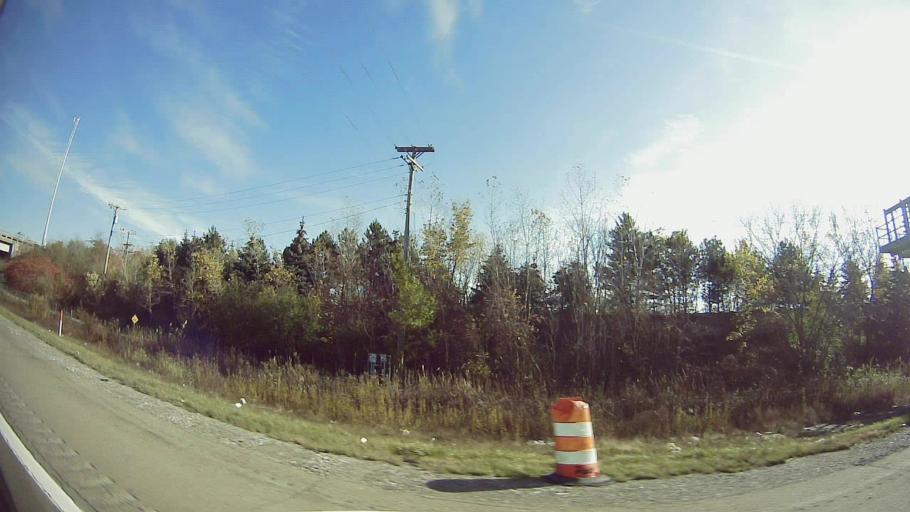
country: US
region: Michigan
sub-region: Wayne County
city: Canton
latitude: 42.2931
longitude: -83.4434
